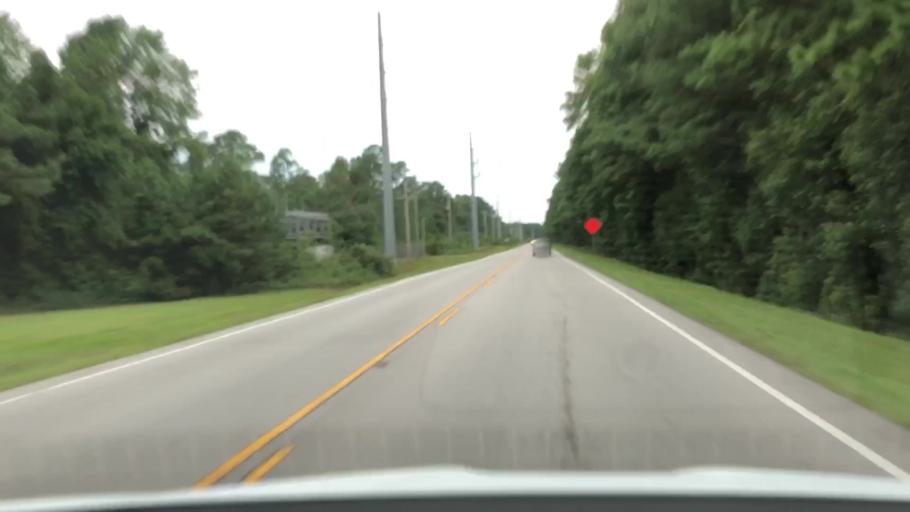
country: US
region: North Carolina
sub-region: Carteret County
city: Cape Carteret
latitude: 34.7408
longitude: -77.0861
